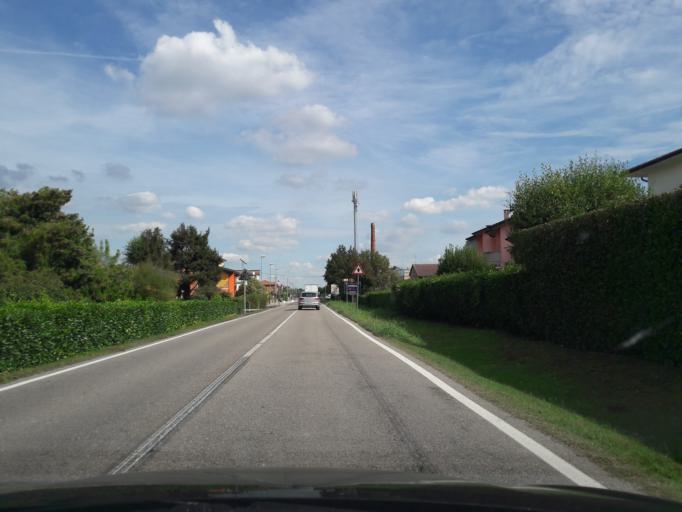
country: IT
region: Veneto
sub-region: Provincia di Rovigo
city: Lendinara
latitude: 45.0883
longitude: 11.5913
